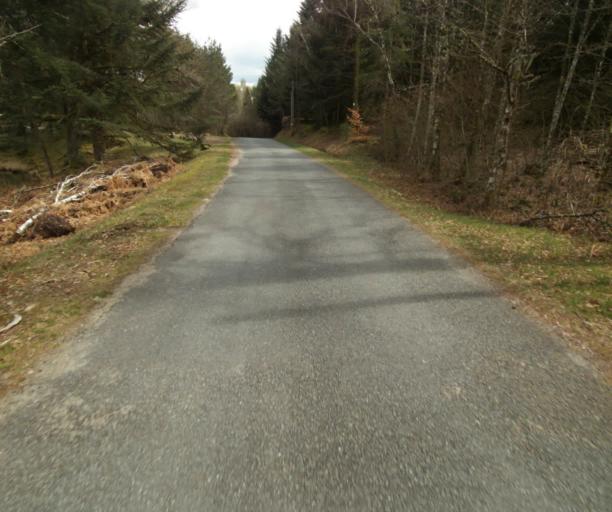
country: FR
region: Limousin
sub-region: Departement de la Correze
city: Correze
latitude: 45.2895
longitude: 1.9553
